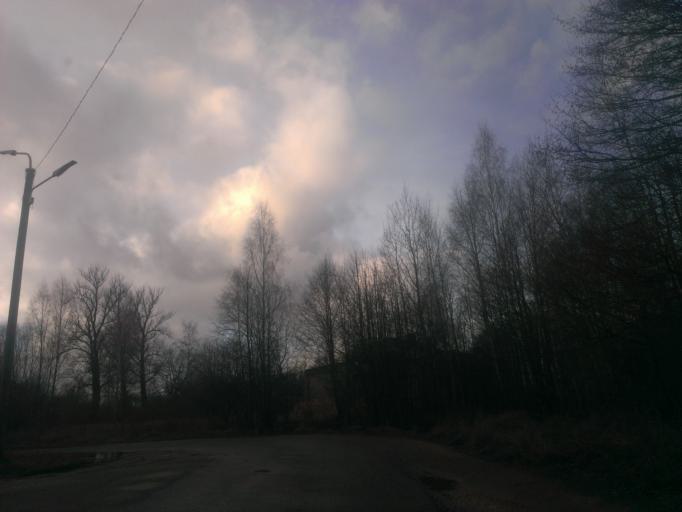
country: LV
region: Riga
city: Daugavgriva
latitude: 57.0613
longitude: 24.0556
